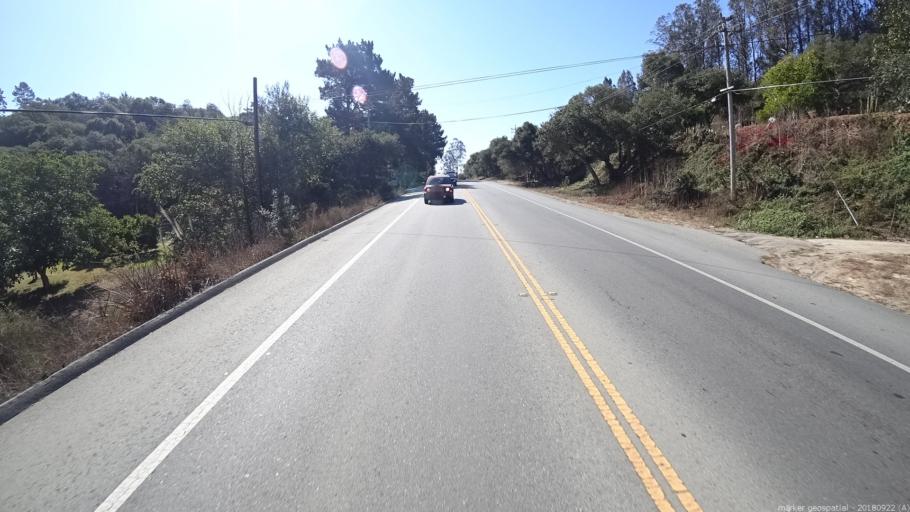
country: US
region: California
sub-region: Monterey County
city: Prunedale
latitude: 36.8326
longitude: -121.6795
